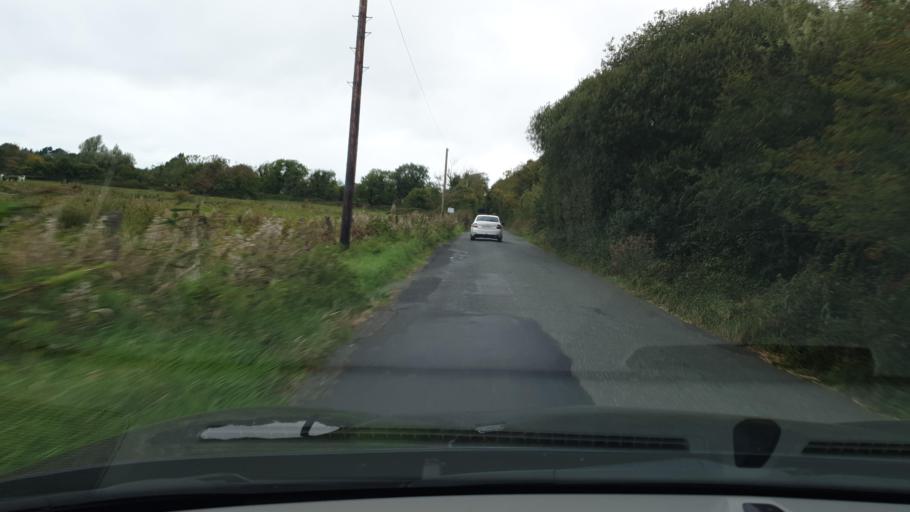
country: IE
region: Leinster
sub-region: An Mhi
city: Dunshaughlin
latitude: 53.5281
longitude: -6.5396
